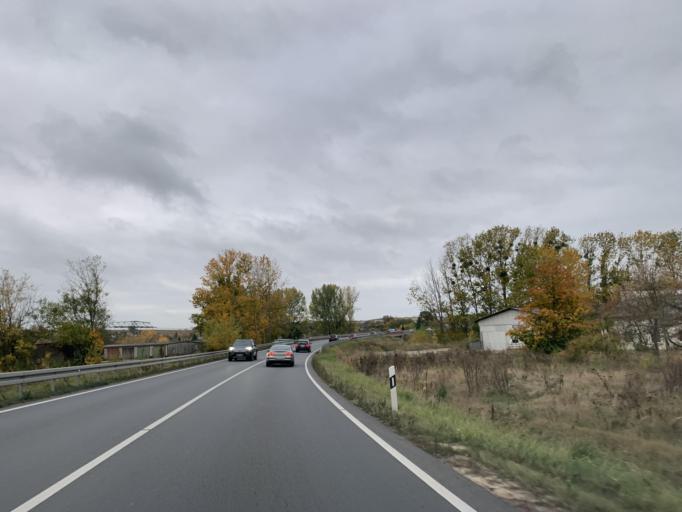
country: DE
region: Mecklenburg-Vorpommern
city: Neubrandenburg
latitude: 53.5386
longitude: 13.2723
